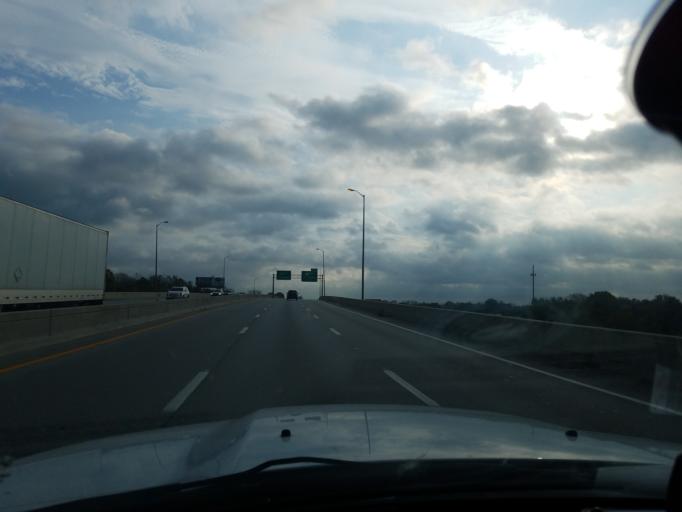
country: US
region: Indiana
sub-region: Floyd County
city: New Albany
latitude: 38.2775
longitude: -85.8022
